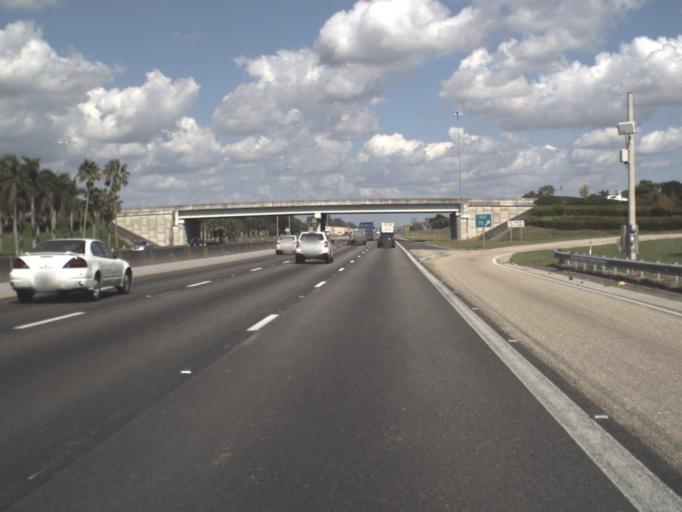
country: US
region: Florida
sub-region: Palm Beach County
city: Boca Del Mar
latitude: 26.3728
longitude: -80.1707
